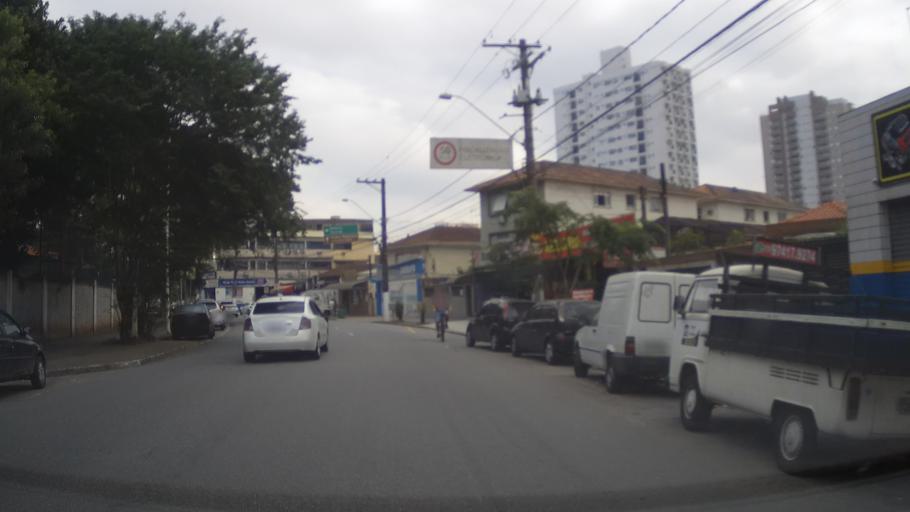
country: BR
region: Sao Paulo
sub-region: Santos
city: Santos
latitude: -23.9647
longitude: -46.3108
